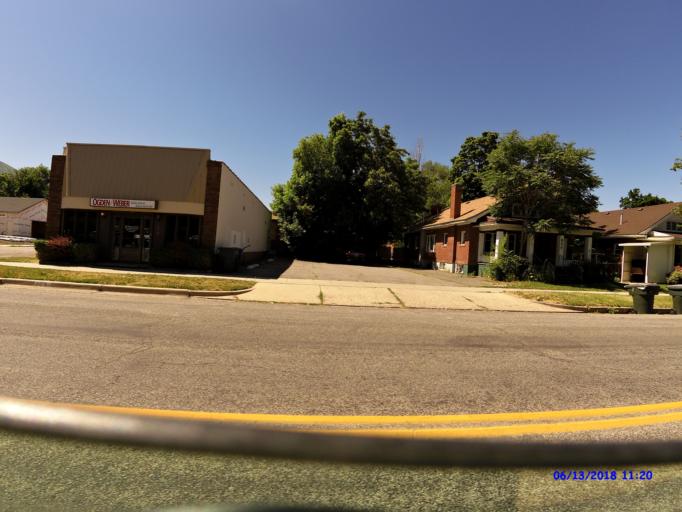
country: US
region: Utah
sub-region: Weber County
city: Ogden
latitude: 41.2205
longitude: -111.9554
